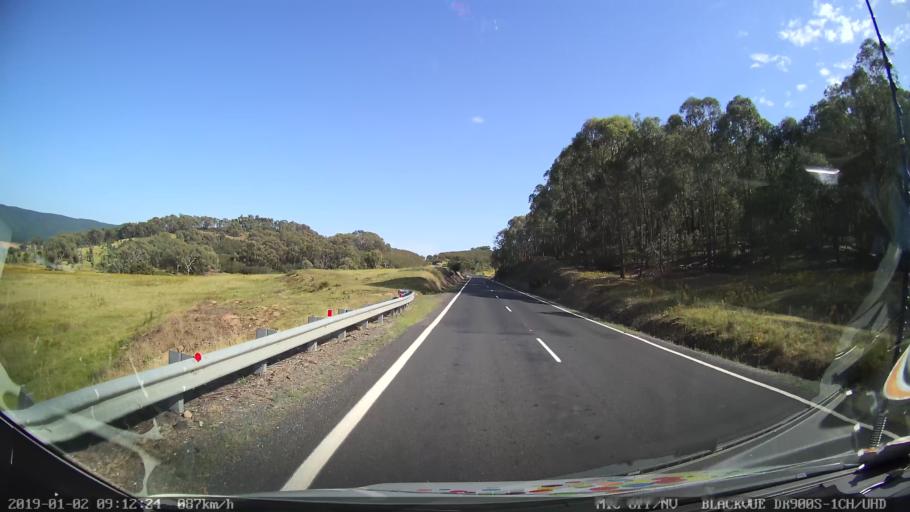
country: AU
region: New South Wales
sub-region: Tumut Shire
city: Tumut
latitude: -35.5007
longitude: 148.2721
